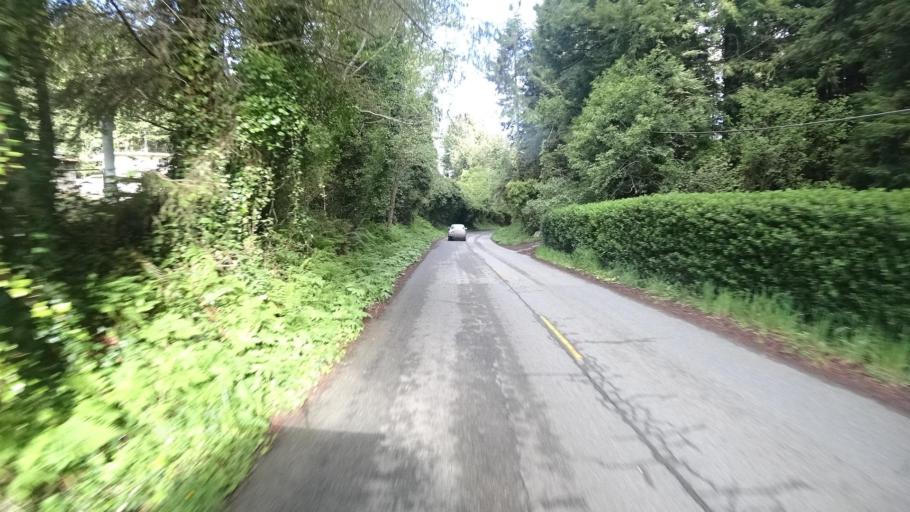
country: US
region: California
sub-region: Humboldt County
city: Westhaven-Moonstone
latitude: 41.0436
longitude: -124.1129
